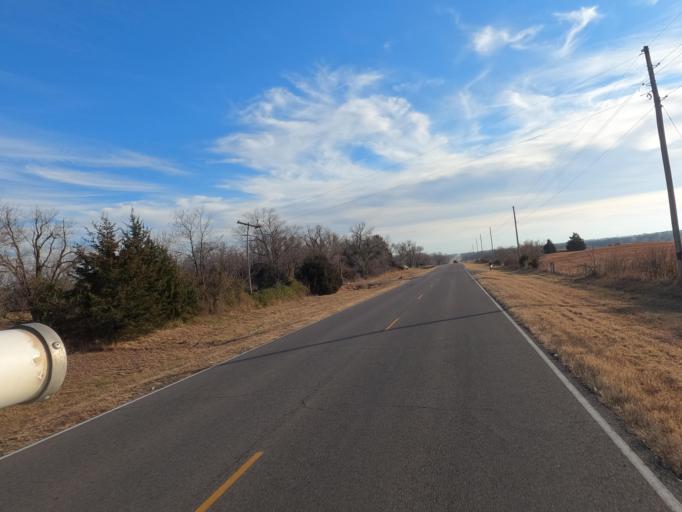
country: US
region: Kansas
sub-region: Reno County
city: Buhler
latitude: 38.0524
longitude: -97.7754
